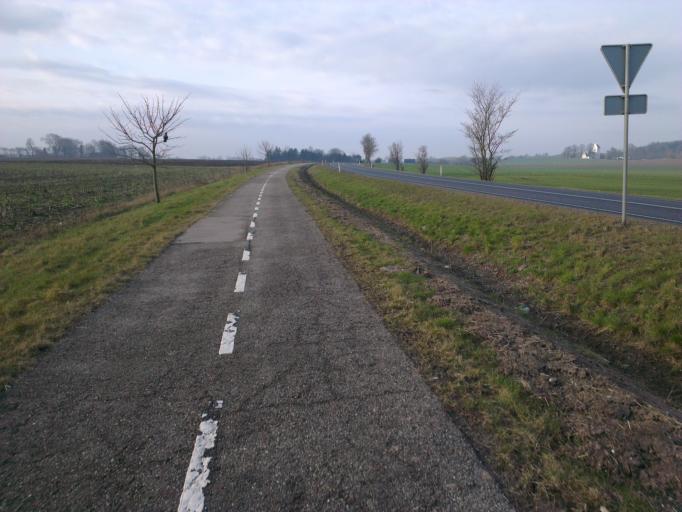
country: DK
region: Capital Region
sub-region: Frederikssund Kommune
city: Skibby
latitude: 55.7885
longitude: 11.9763
